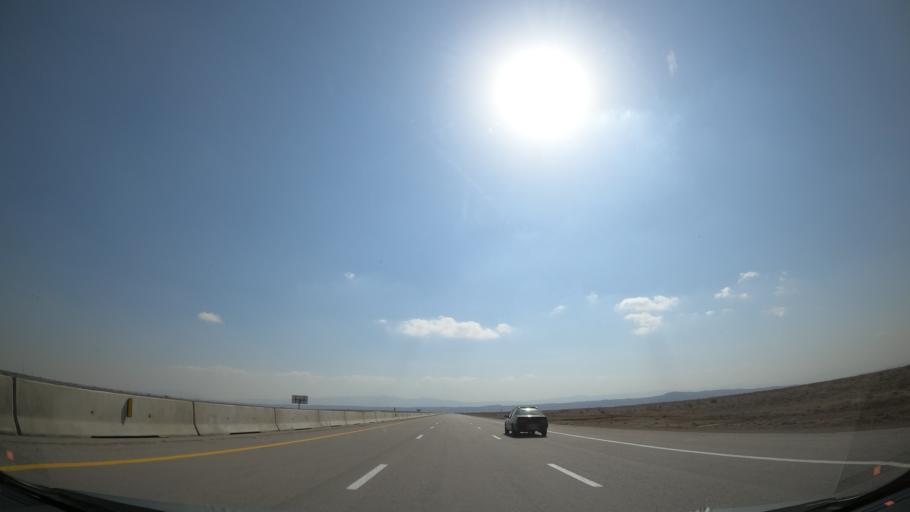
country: IR
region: Alborz
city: Nazarabad
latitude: 35.8585
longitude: 50.4799
